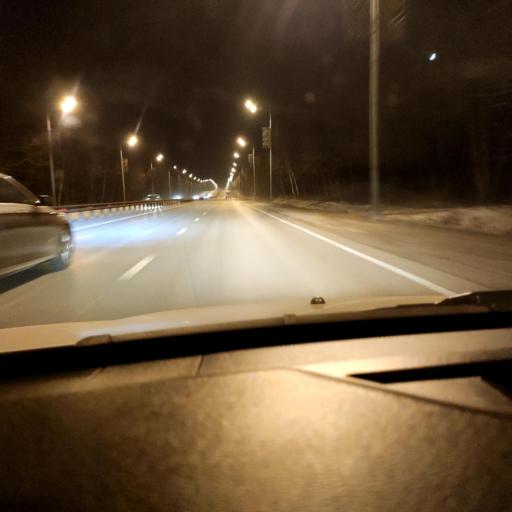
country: RU
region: Samara
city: Novosemeykino
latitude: 53.3276
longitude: 50.2311
